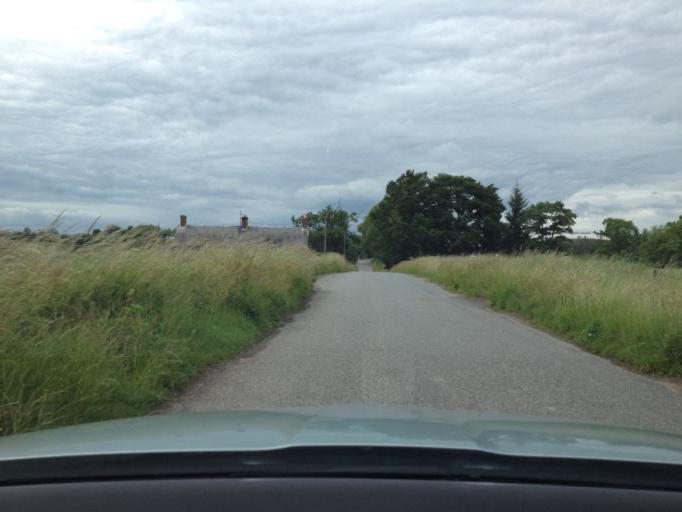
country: GB
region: Scotland
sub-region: Perth and Kinross
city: Bridge of Earn
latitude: 56.3343
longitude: -3.3940
